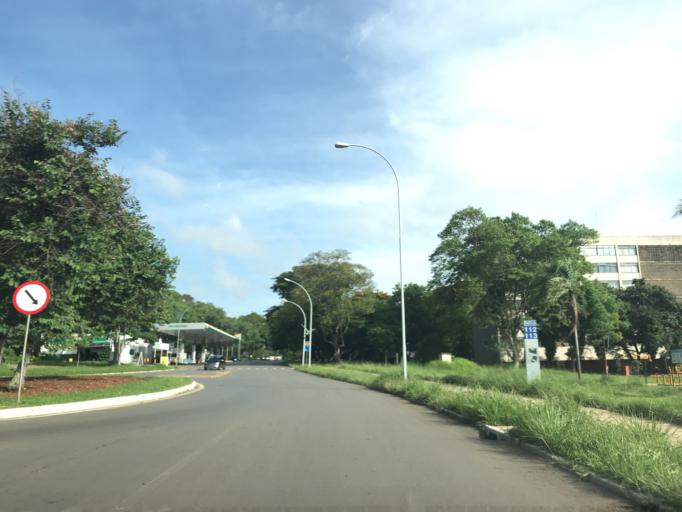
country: BR
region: Federal District
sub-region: Brasilia
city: Brasilia
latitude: -15.7501
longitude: -47.8916
